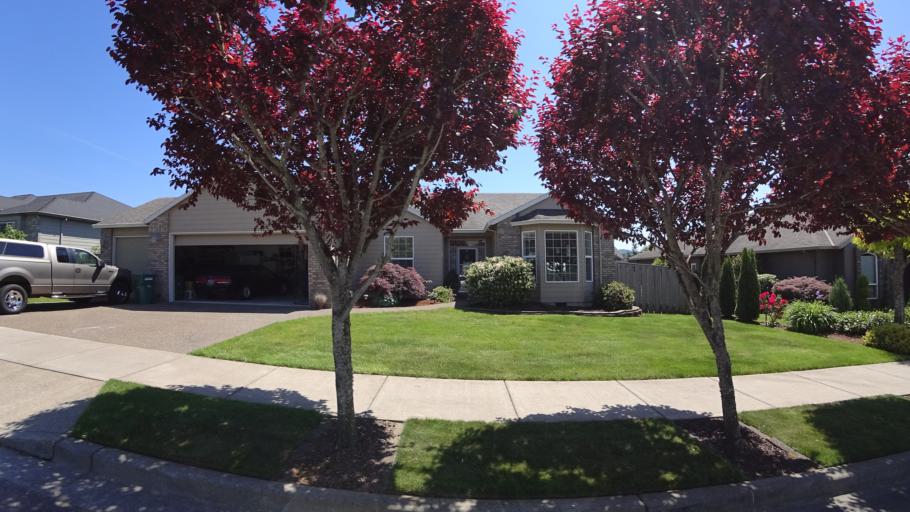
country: US
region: Oregon
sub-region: Clackamas County
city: Happy Valley
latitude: 45.4777
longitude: -122.4871
